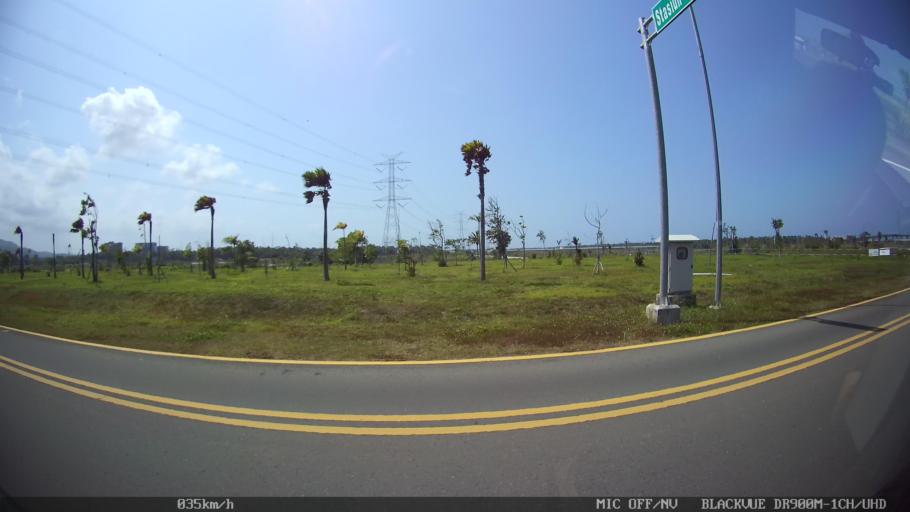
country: ID
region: Daerah Istimewa Yogyakarta
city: Srandakan
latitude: -7.8902
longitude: 110.0630
